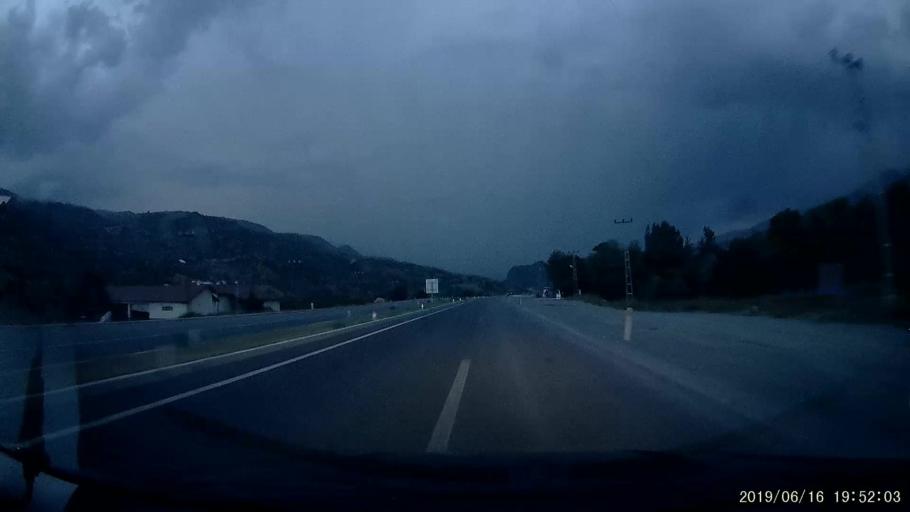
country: TR
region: Sivas
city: Koyulhisar
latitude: 40.2851
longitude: 37.8104
